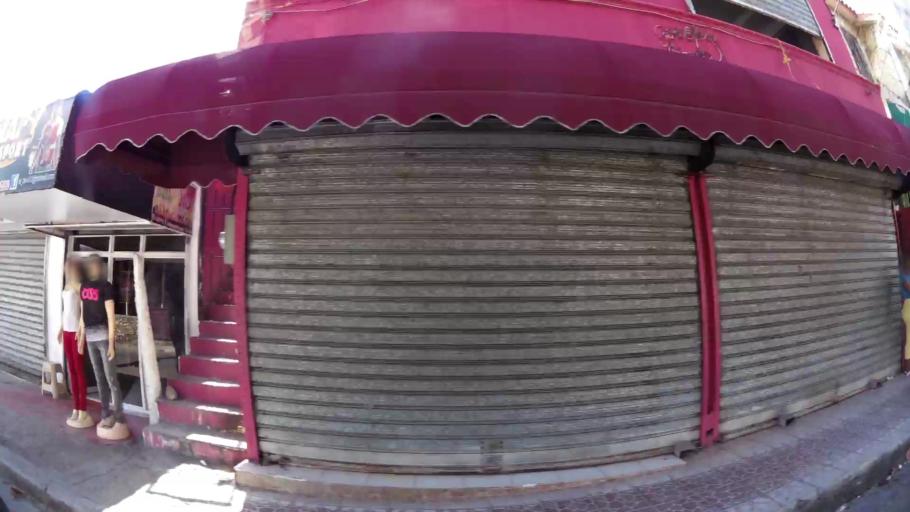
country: DO
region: San Cristobal
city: San Cristobal
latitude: 18.4282
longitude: -70.0852
